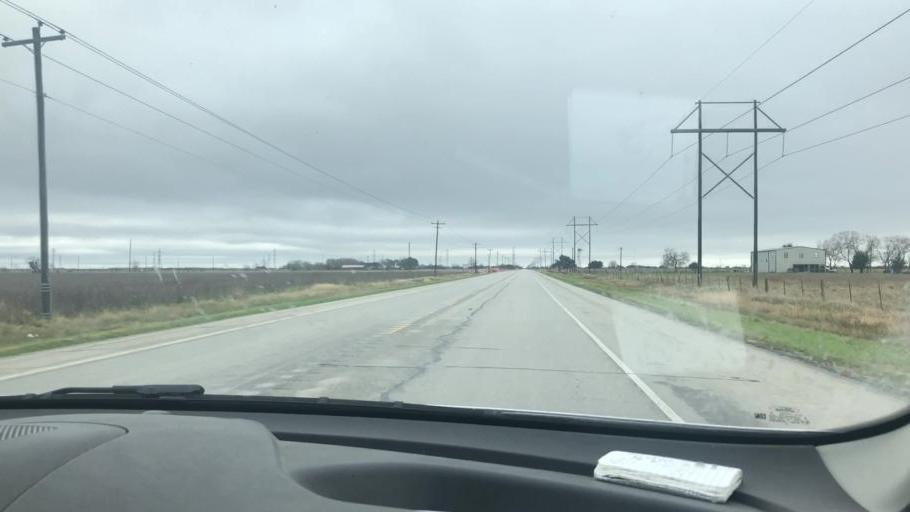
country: US
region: Texas
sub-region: Wharton County
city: Boling
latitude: 29.1880
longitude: -96.0127
